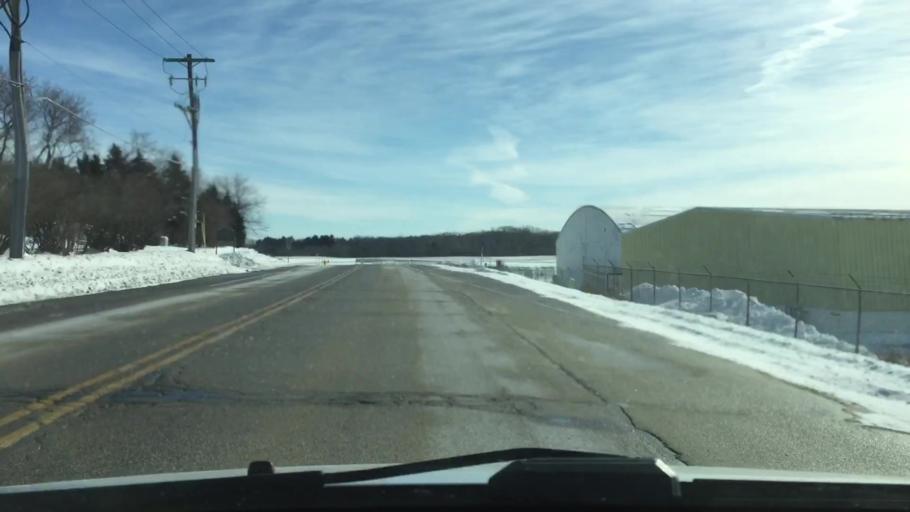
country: US
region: Wisconsin
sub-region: Waukesha County
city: Waukesha
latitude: 43.0435
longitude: -88.2299
